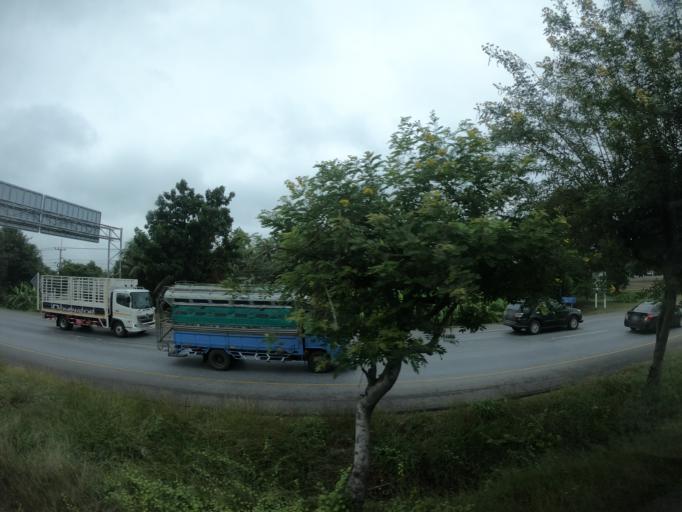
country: TH
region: Nakhon Ratchasima
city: Non Daeng
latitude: 15.3422
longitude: 102.4432
